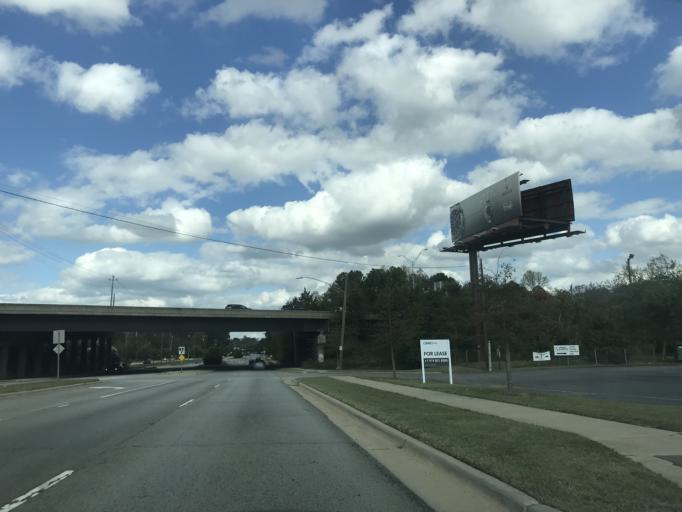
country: US
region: North Carolina
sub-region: Wake County
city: Raleigh
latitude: 35.7534
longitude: -78.6414
